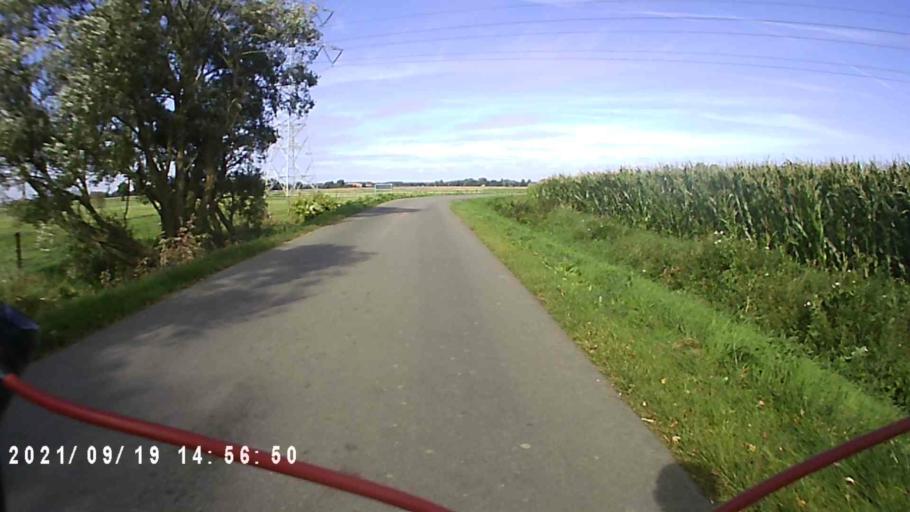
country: DE
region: Lower Saxony
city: Bunde
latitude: 53.1456
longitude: 7.2081
